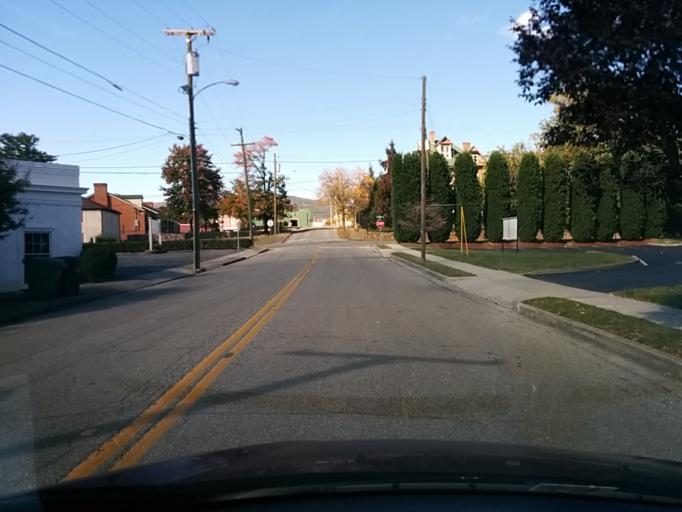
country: US
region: Virginia
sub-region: City of Salem
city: Salem
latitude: 37.2912
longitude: -80.0553
